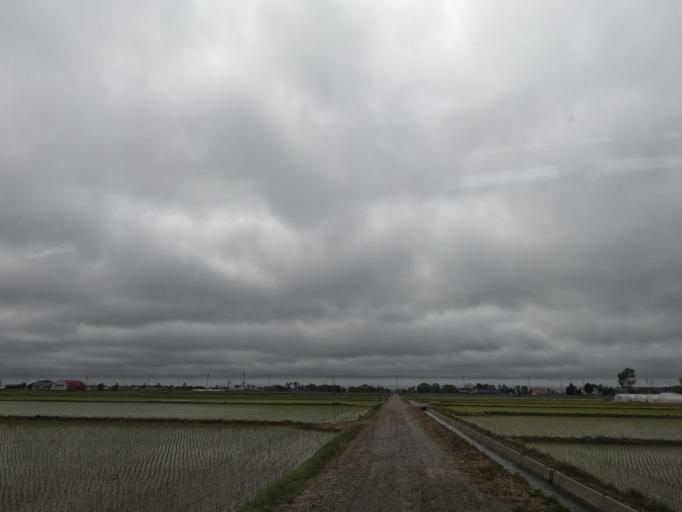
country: JP
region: Hokkaido
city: Tobetsu
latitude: 43.2463
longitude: 141.5194
